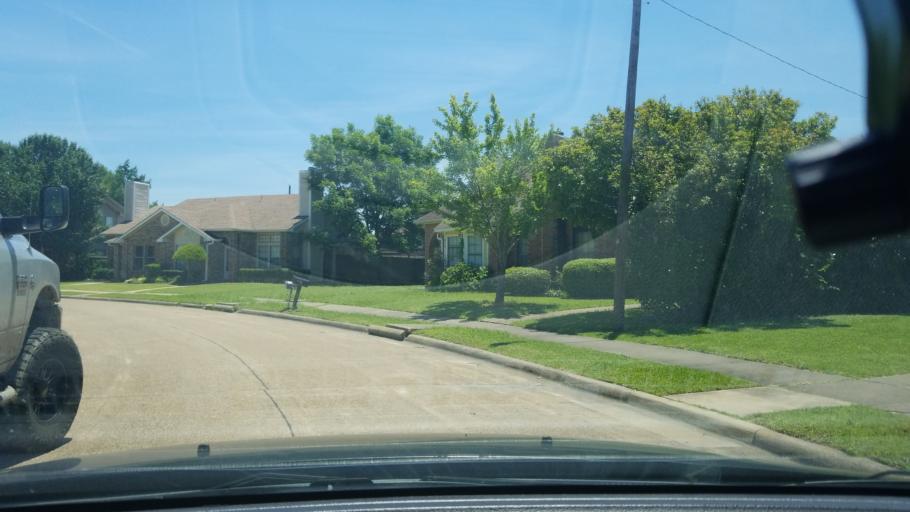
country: US
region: Texas
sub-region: Dallas County
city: Mesquite
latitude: 32.7730
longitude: -96.6074
